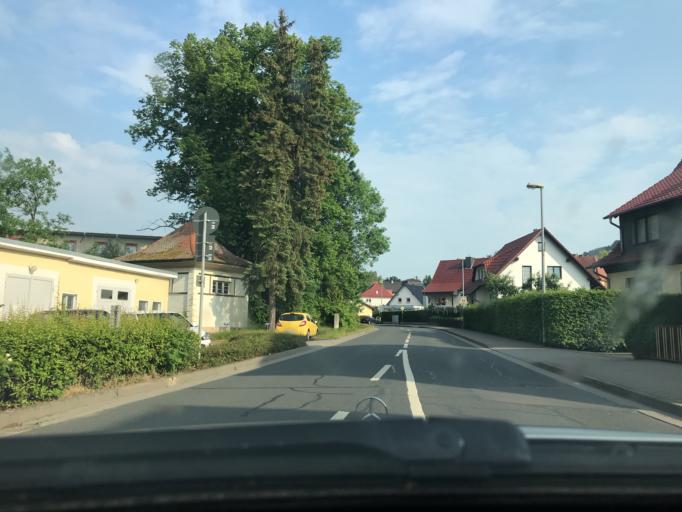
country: DE
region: Thuringia
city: Heilbad Heiligenstadt
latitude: 51.3750
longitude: 10.1425
